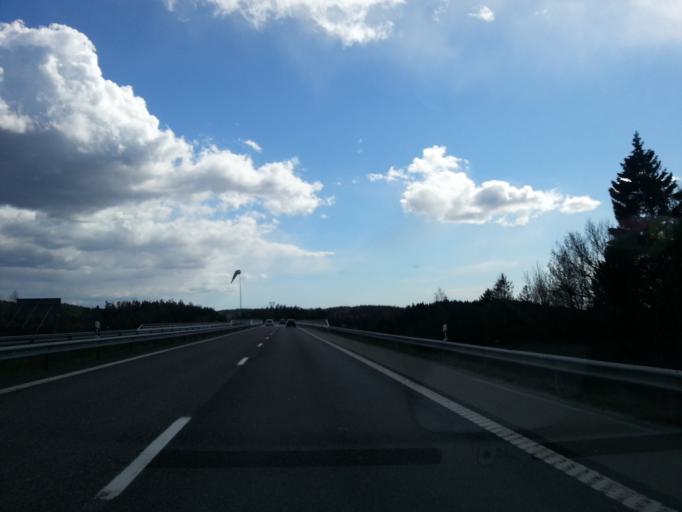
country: SE
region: Vaestra Goetaland
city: Svanesund
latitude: 58.1135
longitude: 11.8791
